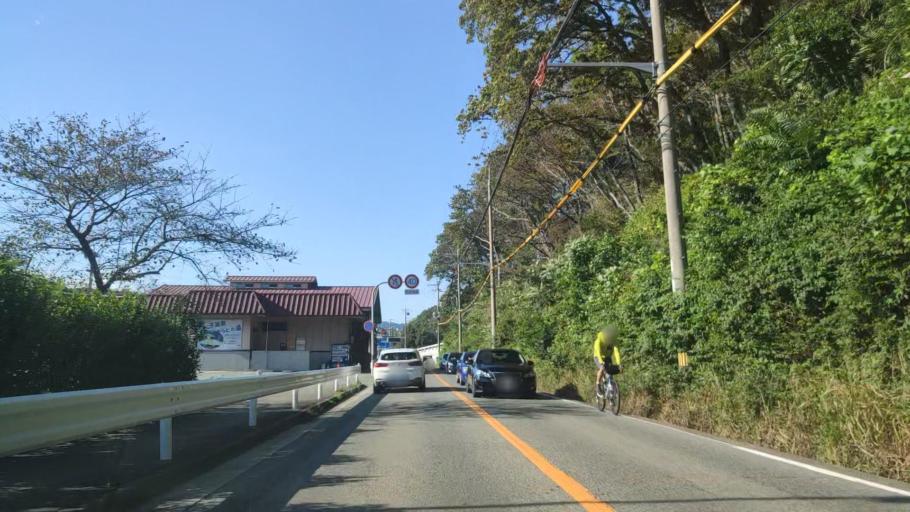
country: JP
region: Hyogo
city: Sandacho
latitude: 34.7901
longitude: 135.2108
